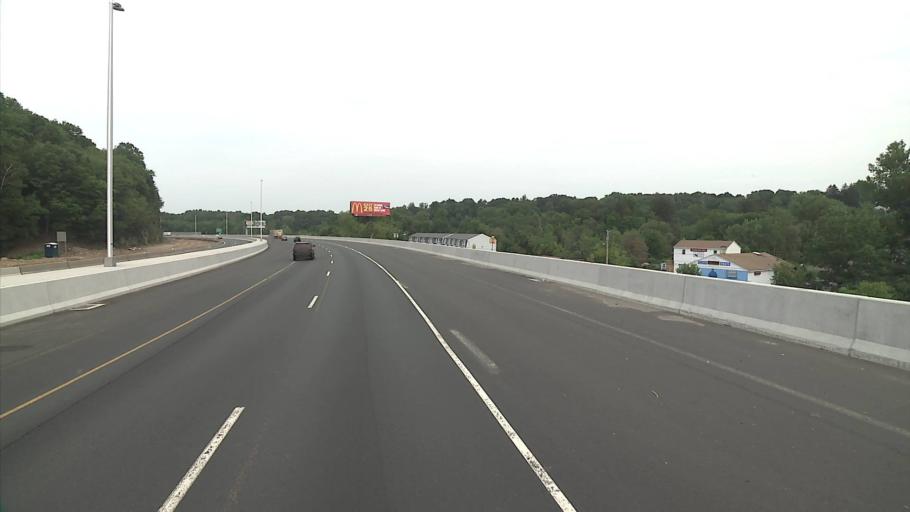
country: US
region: Connecticut
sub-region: New Haven County
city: Prospect
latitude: 41.5436
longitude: -72.9818
